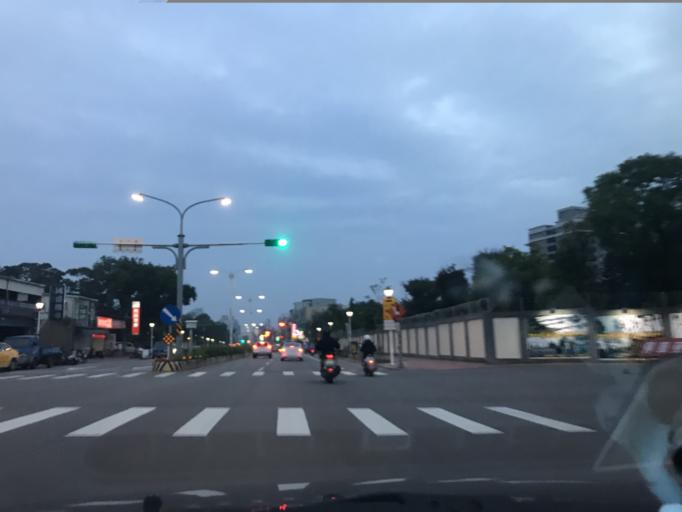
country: TW
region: Taiwan
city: Daxi
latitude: 24.9318
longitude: 121.2382
